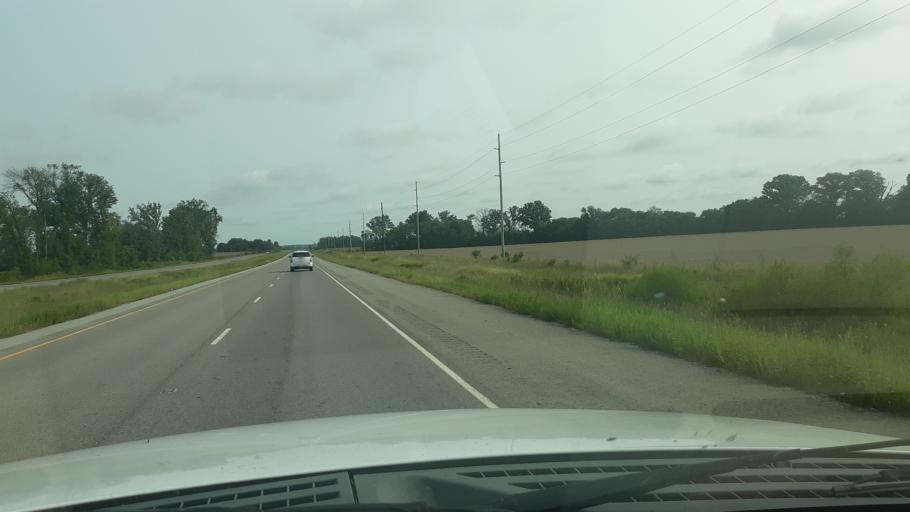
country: US
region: Illinois
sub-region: Saline County
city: Eldorado
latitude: 37.8416
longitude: -88.4149
